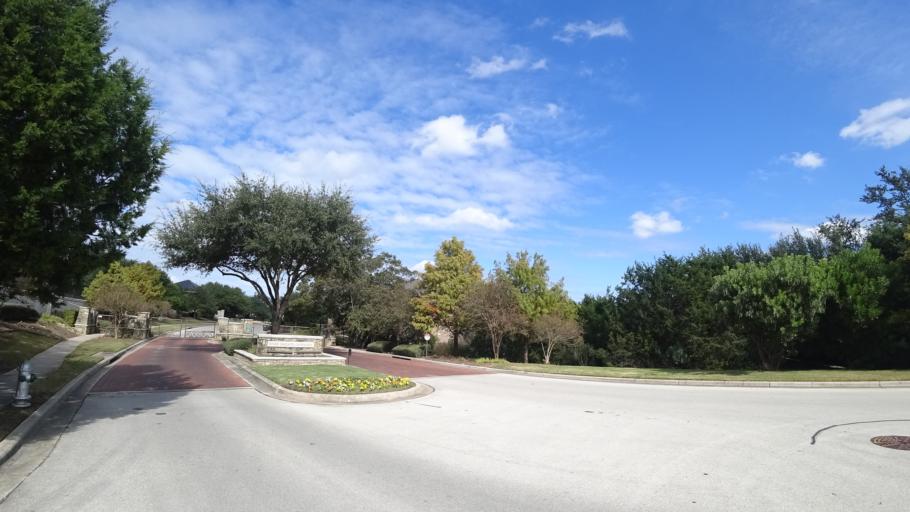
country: US
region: Texas
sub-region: Travis County
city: Hudson Bend
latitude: 30.3680
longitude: -97.9066
